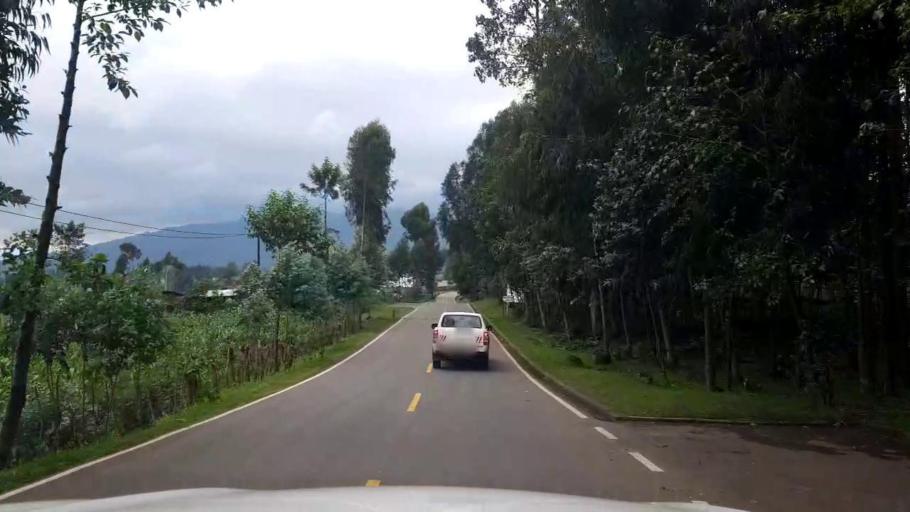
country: RW
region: Northern Province
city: Musanze
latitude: -1.4348
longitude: 29.5559
